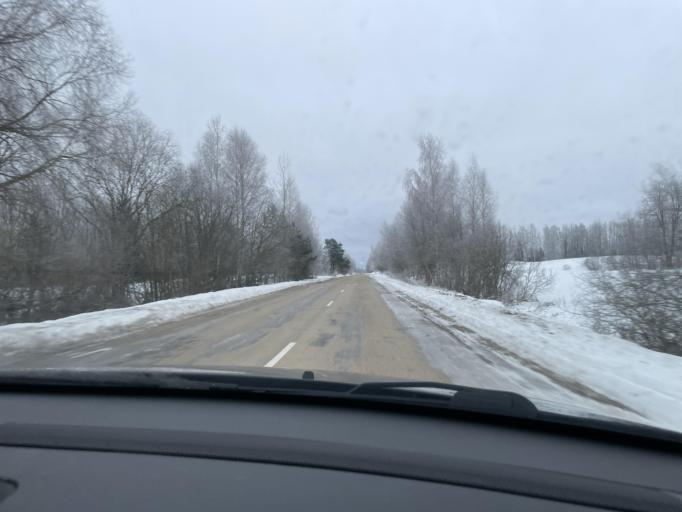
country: LV
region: Ludzas Rajons
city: Ludza
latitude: 56.4376
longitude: 27.5283
